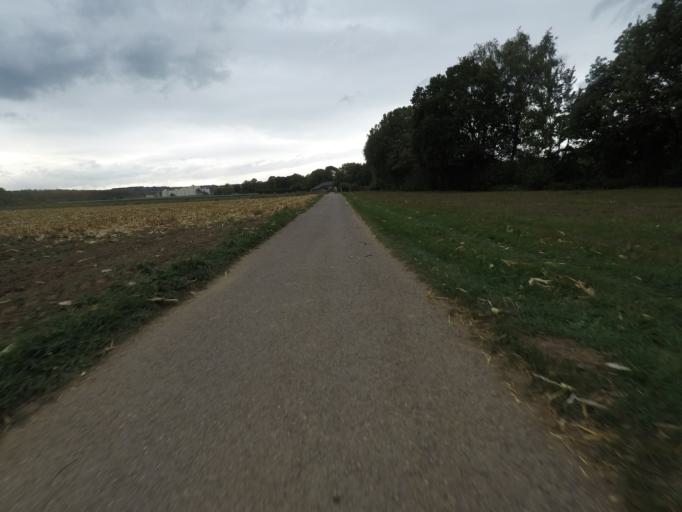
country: DE
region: Baden-Wuerttemberg
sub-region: Regierungsbezirk Stuttgart
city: Leinfelden-Echterdingen
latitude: 48.7170
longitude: 9.1359
